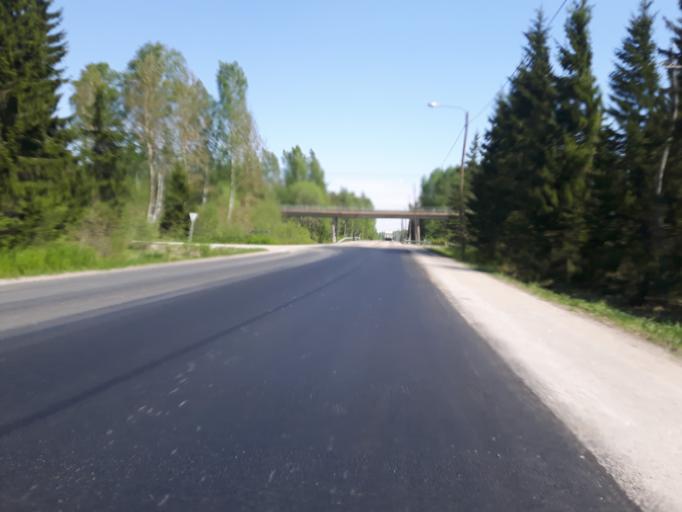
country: FI
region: Uusimaa
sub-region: Helsinki
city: Pornainen
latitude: 60.3277
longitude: 25.4367
